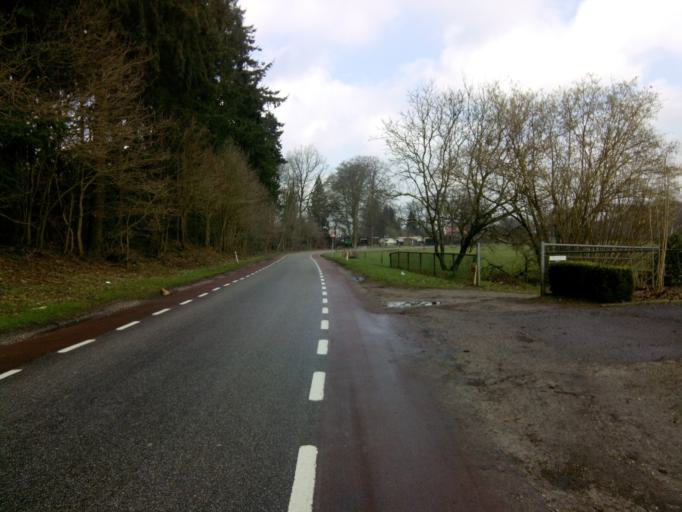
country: NL
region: Utrecht
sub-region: Gemeente Utrechtse Heuvelrug
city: Overberg
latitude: 52.0339
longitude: 5.4895
